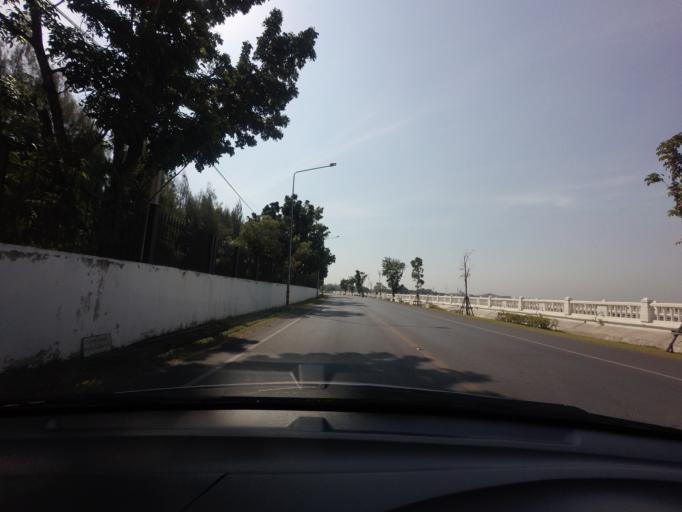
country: TH
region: Bangkok
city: Sai Mai
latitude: 13.9303
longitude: 100.6211
